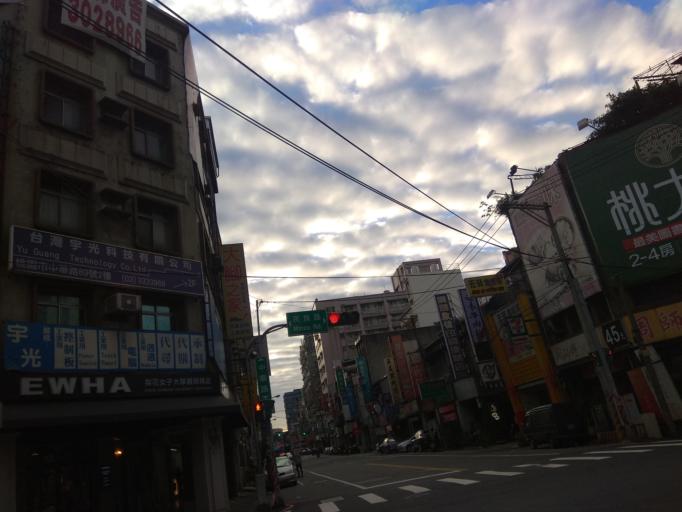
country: TW
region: Taiwan
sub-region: Taoyuan
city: Taoyuan
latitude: 24.9904
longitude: 121.3098
